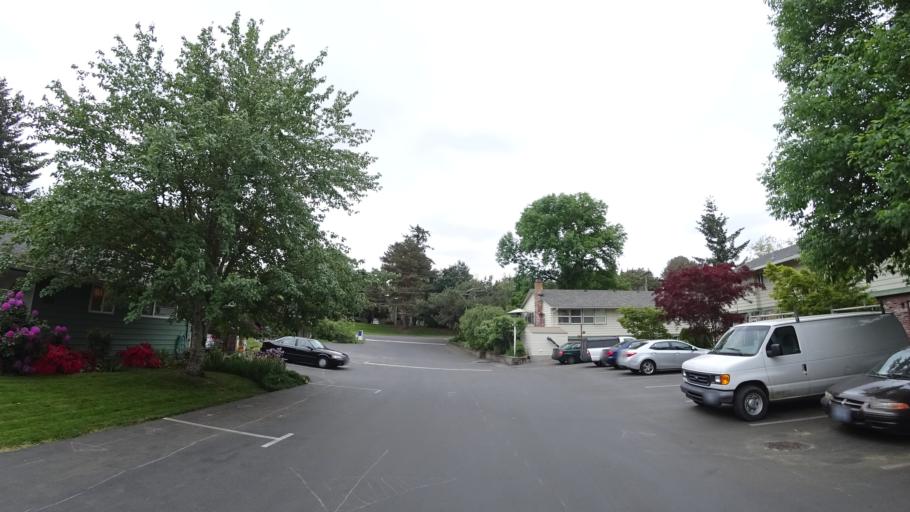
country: US
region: Oregon
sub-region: Washington County
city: Raleigh Hills
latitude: 45.4771
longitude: -122.7499
